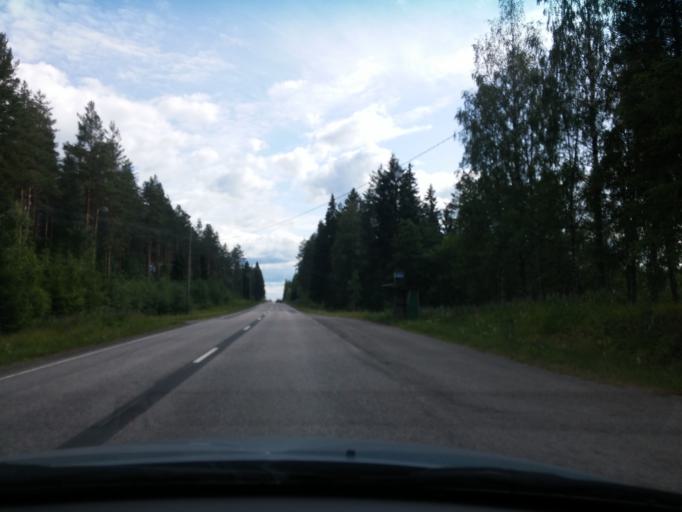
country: FI
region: Central Finland
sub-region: Keuruu
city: Keuruu
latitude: 62.3311
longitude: 24.7327
